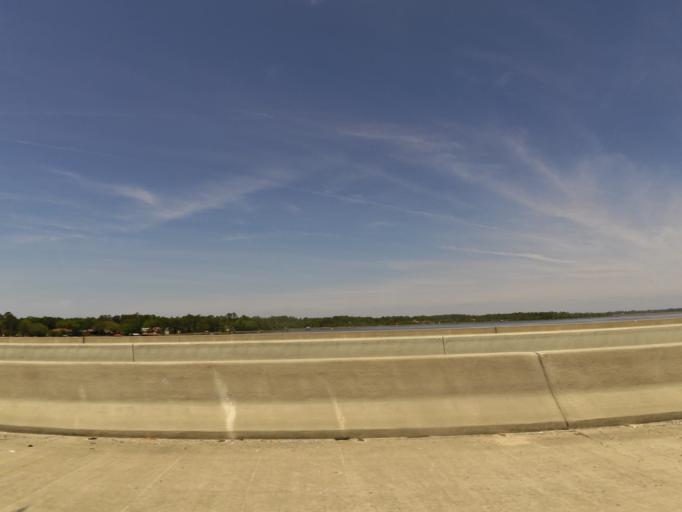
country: US
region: Georgia
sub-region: Glynn County
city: Dock Junction
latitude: 31.1911
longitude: -81.5406
